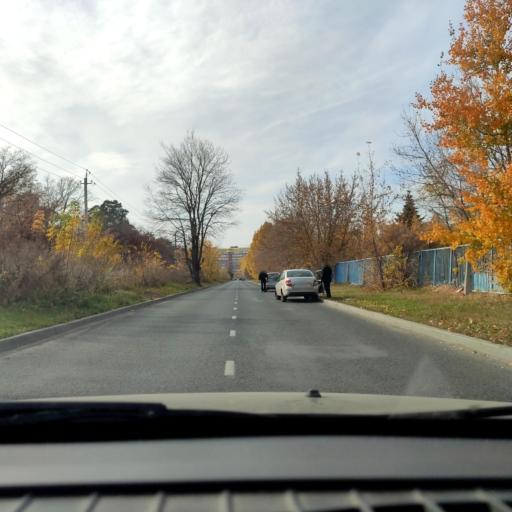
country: RU
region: Samara
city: Tol'yatti
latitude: 53.5200
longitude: 49.3239
